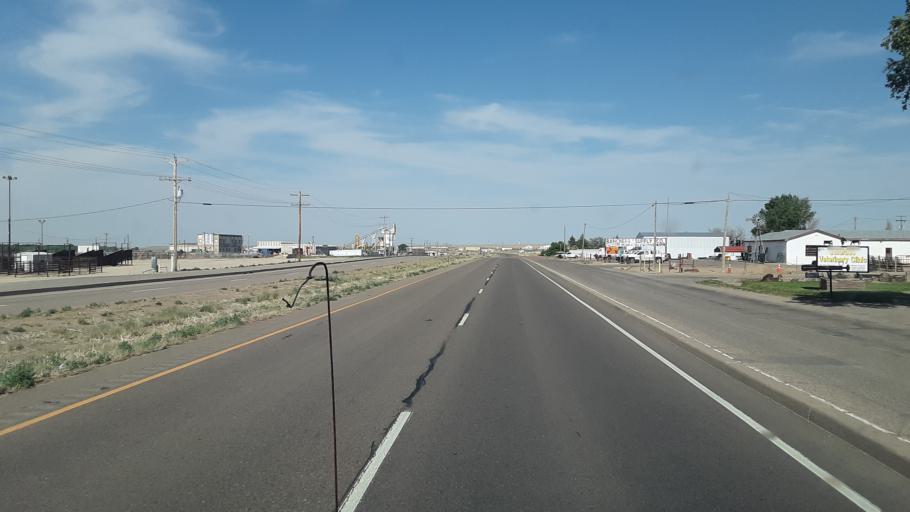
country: US
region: Colorado
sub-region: Otero County
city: La Junta
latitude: 37.9862
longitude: -103.5194
